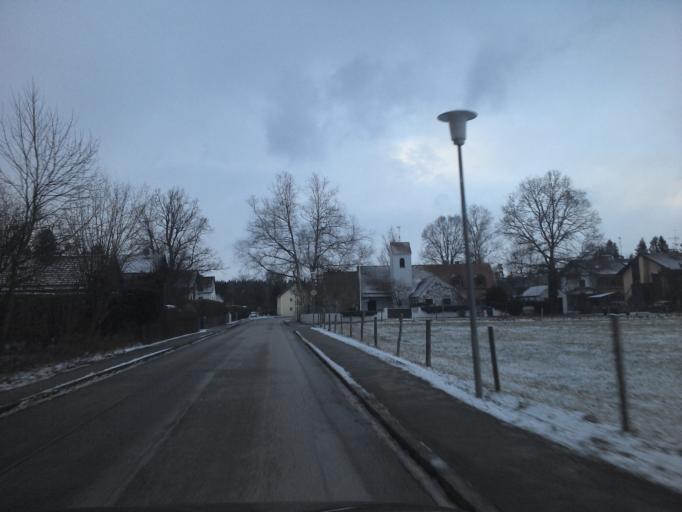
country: DE
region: Bavaria
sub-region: Upper Bavaria
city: Seeshaupt
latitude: 47.8237
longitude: 11.2874
